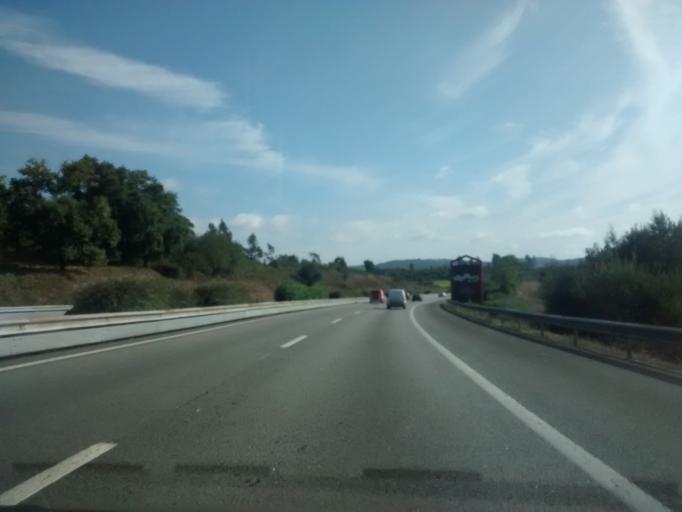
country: PT
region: Porto
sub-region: Santo Tirso
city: Santo Tirso
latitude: 41.3618
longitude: -8.5001
